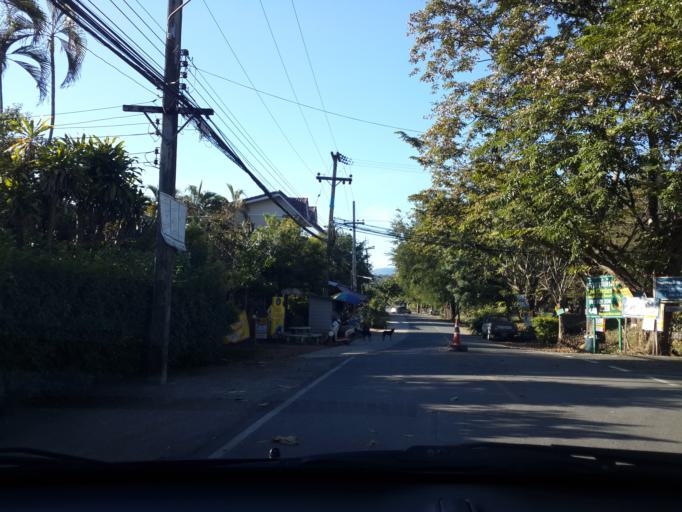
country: TH
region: Chiang Mai
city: San Sai
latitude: 18.9091
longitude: 99.1320
